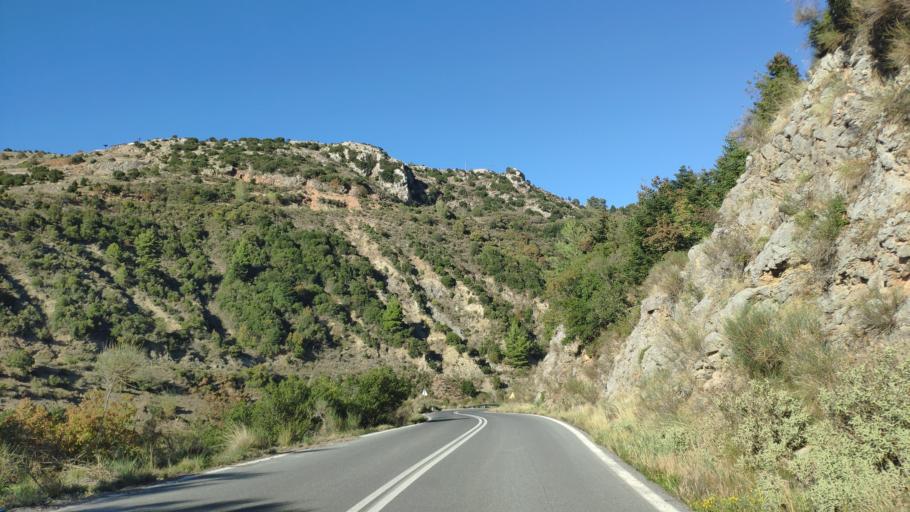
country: GR
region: Peloponnese
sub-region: Nomos Arkadias
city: Dimitsana
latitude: 37.5789
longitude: 22.0614
